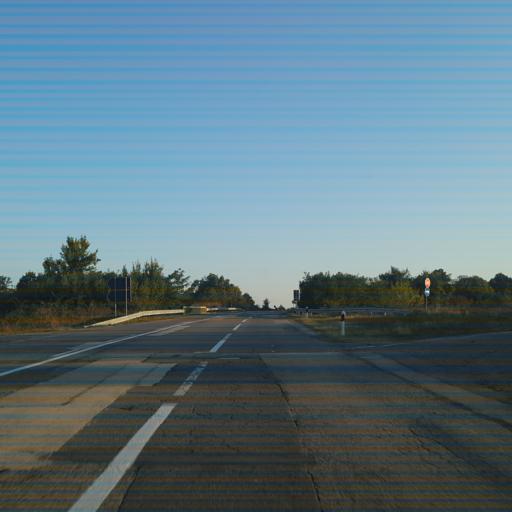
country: RS
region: Central Serbia
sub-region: Borski Okrug
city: Negotin
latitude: 44.1224
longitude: 22.3405
